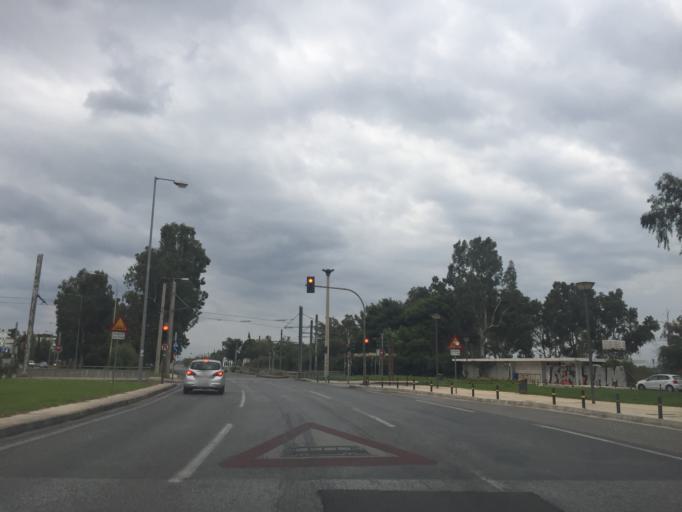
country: GR
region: Attica
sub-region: Nomarchia Athinas
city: Glyfada
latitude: 37.8540
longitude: 23.7517
